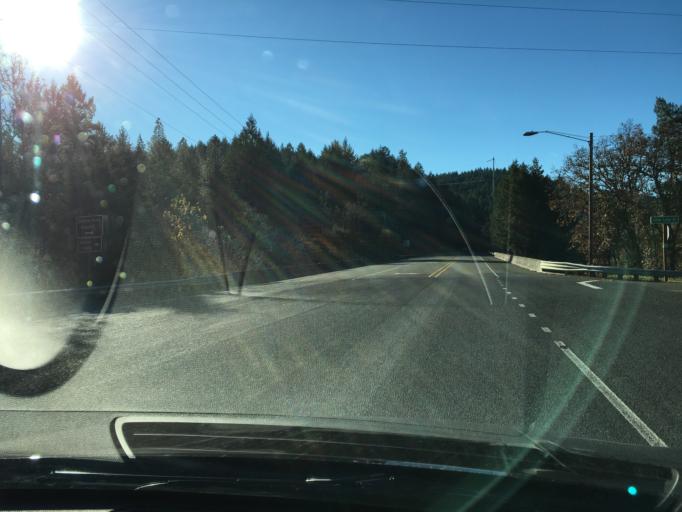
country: US
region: Oregon
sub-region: Douglas County
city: Glide
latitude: 43.2976
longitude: -123.1003
